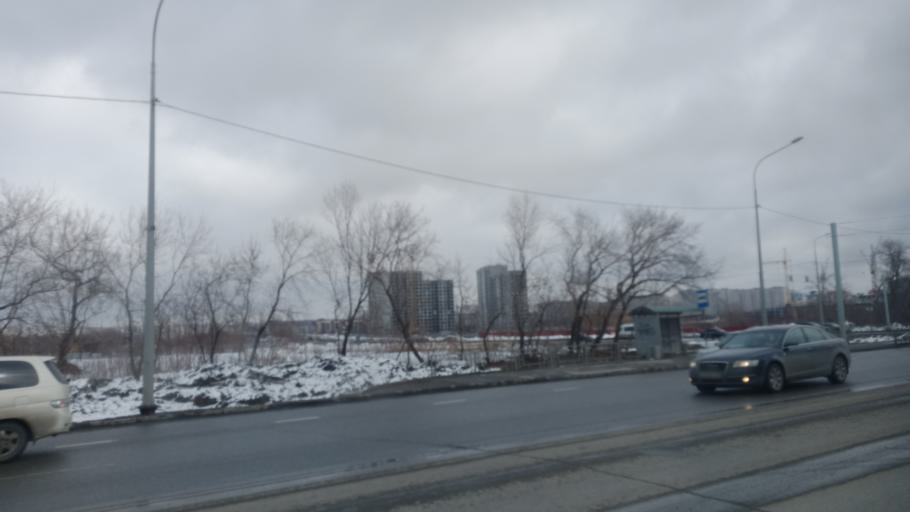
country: RU
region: Altai Krai
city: Novosilikatnyy
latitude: 53.3466
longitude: 83.6486
